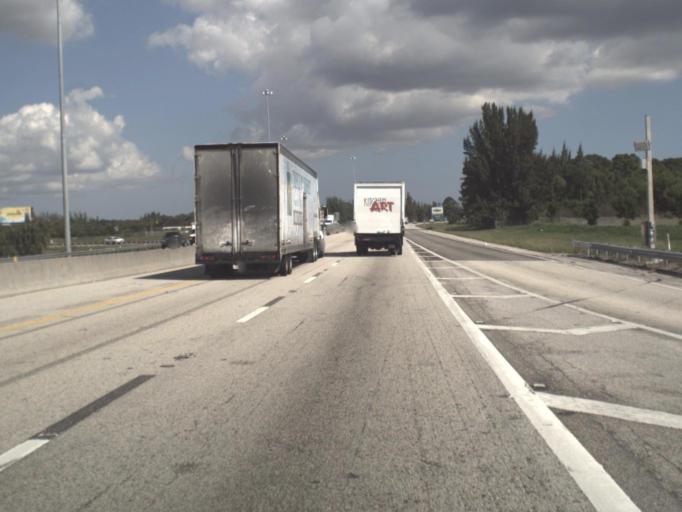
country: US
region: Florida
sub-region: Palm Beach County
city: Lake Belvedere Estates
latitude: 26.6830
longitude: -80.1637
